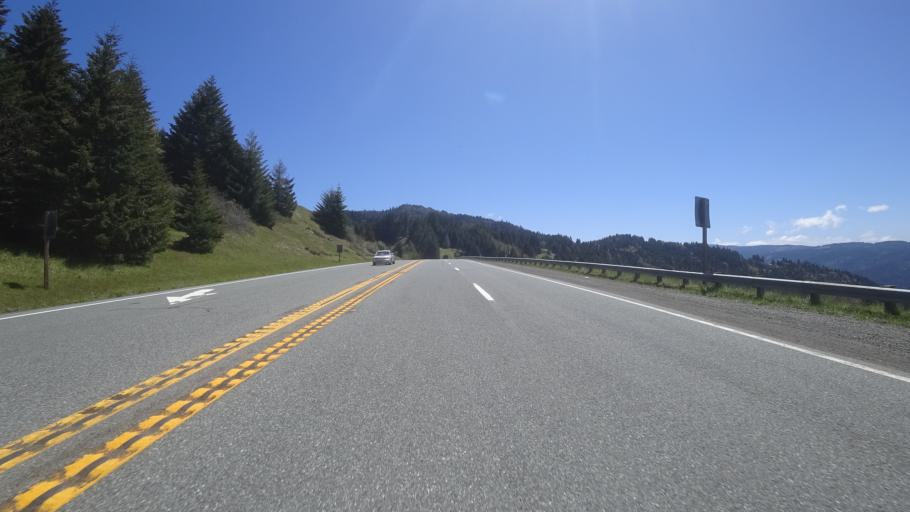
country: US
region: California
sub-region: Humboldt County
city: Willow Creek
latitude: 40.8984
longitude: -123.7750
